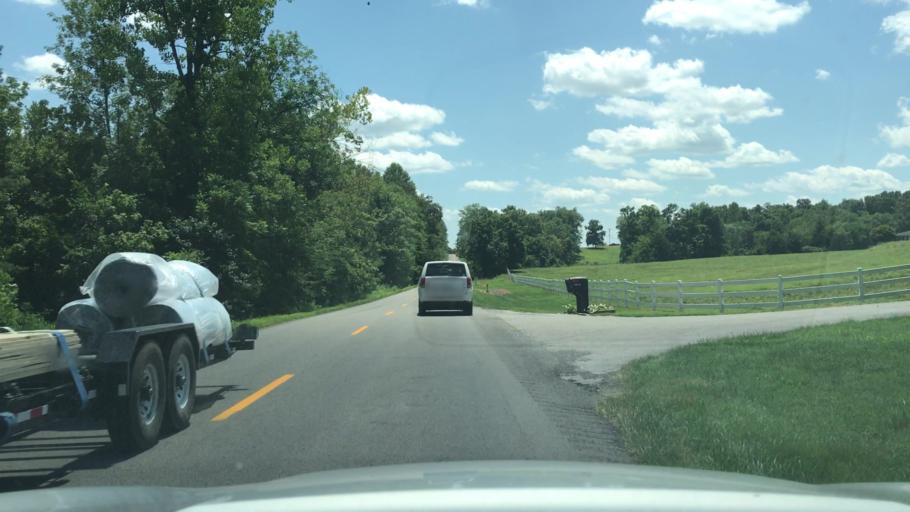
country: US
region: Kentucky
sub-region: Christian County
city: Hopkinsville
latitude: 36.9093
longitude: -87.4441
